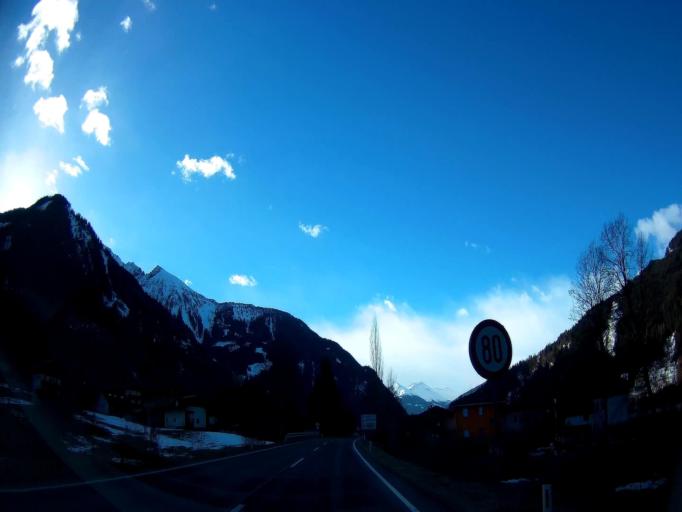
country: AT
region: Salzburg
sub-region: Politischer Bezirk Sankt Johann im Pongau
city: Dorfgastein
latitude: 47.2203
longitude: 13.1090
